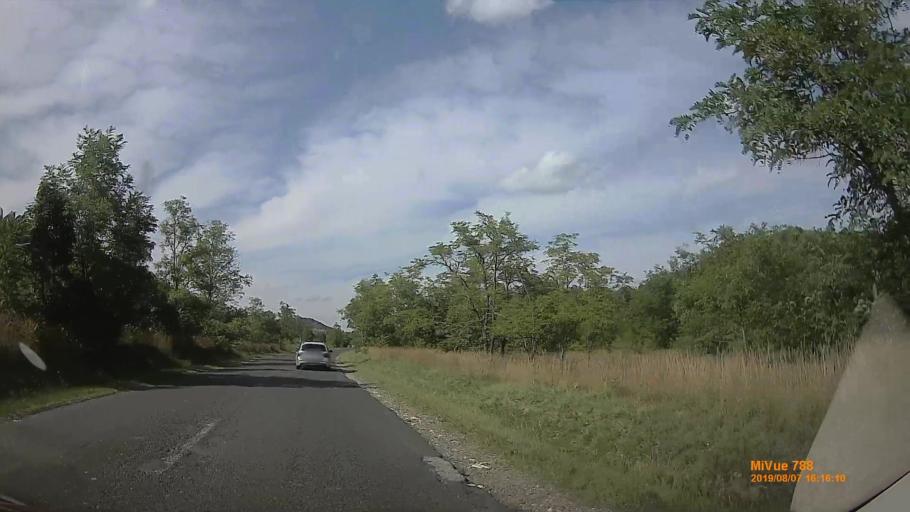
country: HU
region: Zala
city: Gyenesdias
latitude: 46.8095
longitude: 17.2703
